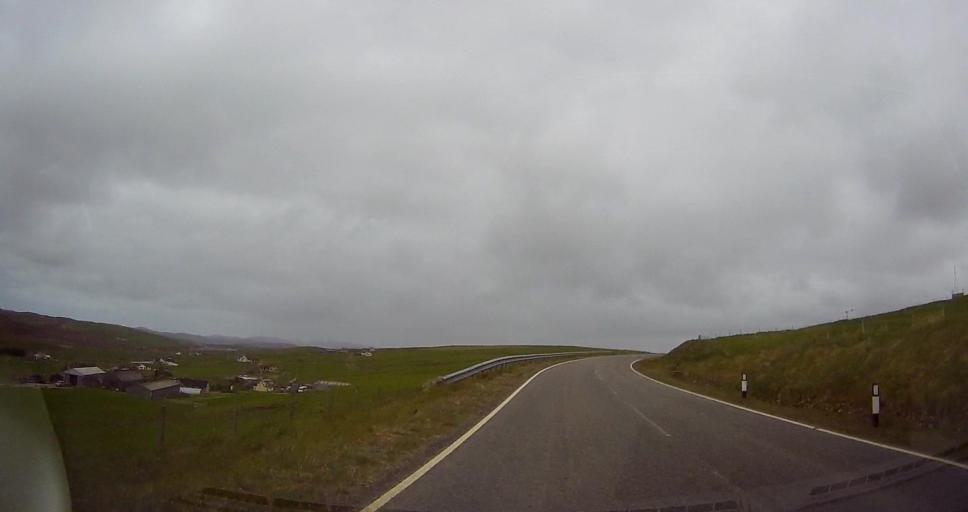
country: GB
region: Scotland
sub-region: Shetland Islands
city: Lerwick
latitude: 60.2604
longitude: -1.4055
